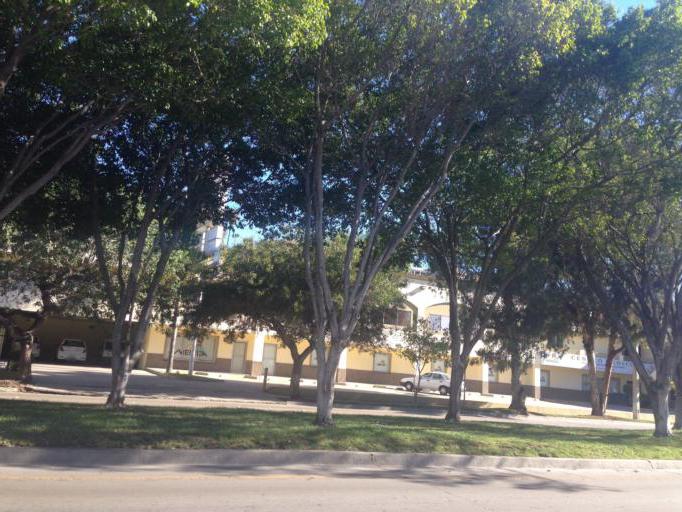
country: MX
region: Baja California
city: Tijuana
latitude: 32.5264
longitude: -117.0097
